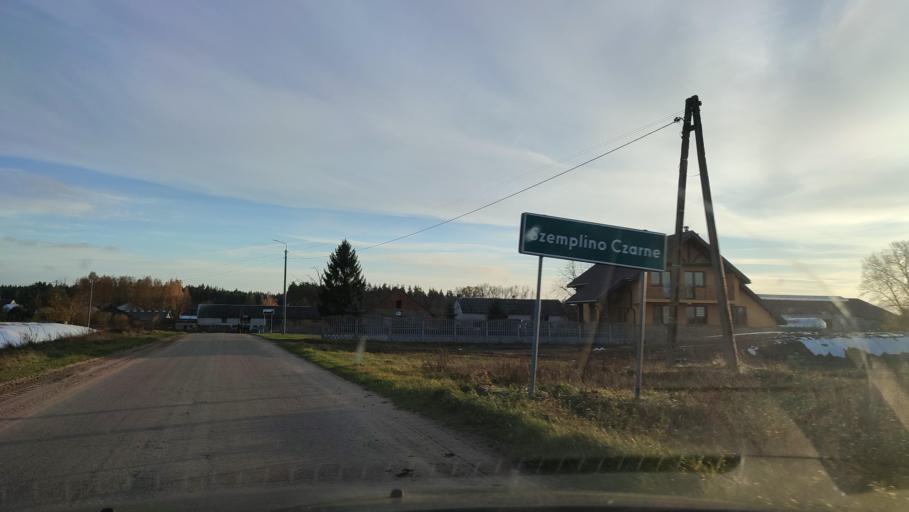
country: PL
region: Masovian Voivodeship
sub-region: Powiat mlawski
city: Dzierzgowo
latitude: 53.2702
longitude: 20.6450
